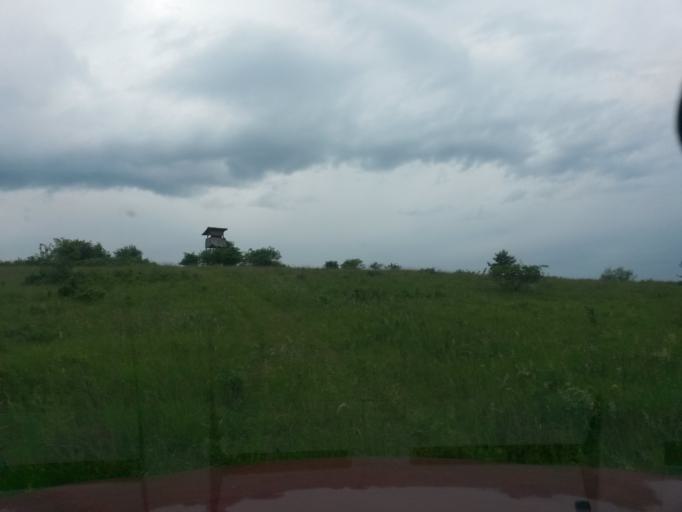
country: SK
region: Kosicky
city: Kosice
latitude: 48.7025
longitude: 21.1651
